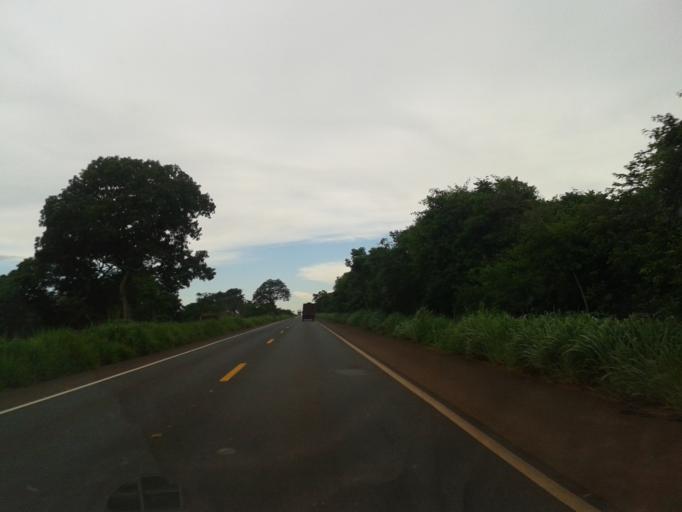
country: BR
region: Minas Gerais
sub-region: Santa Vitoria
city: Santa Vitoria
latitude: -18.8882
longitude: -50.1559
